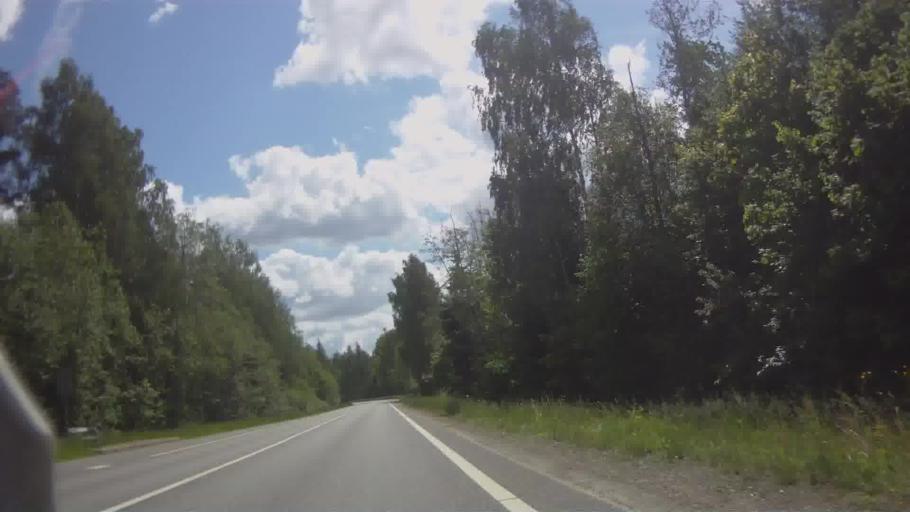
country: LV
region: Livani
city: Livani
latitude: 56.5234
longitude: 26.1603
